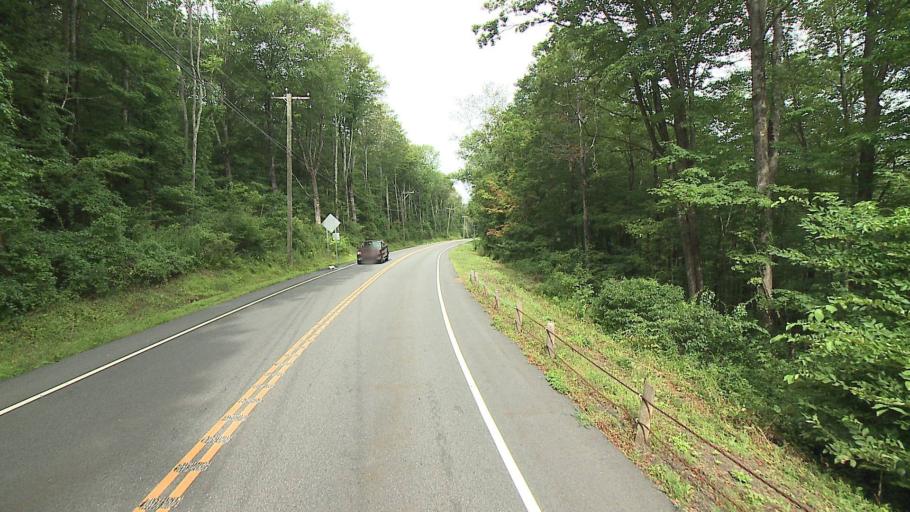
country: US
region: Connecticut
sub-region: Litchfield County
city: New Preston
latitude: 41.7145
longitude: -73.3193
